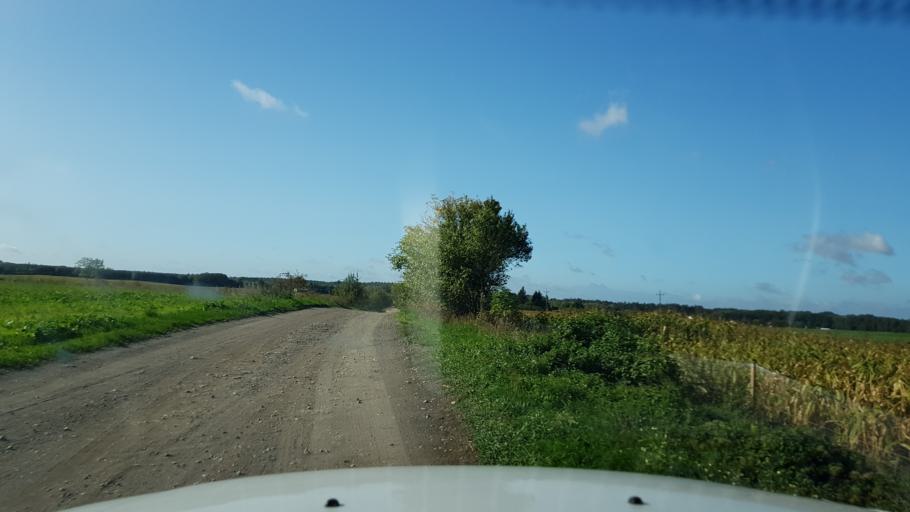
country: PL
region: West Pomeranian Voivodeship
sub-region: Powiat pyrzycki
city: Lipiany
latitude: 53.0115
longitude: 14.9304
